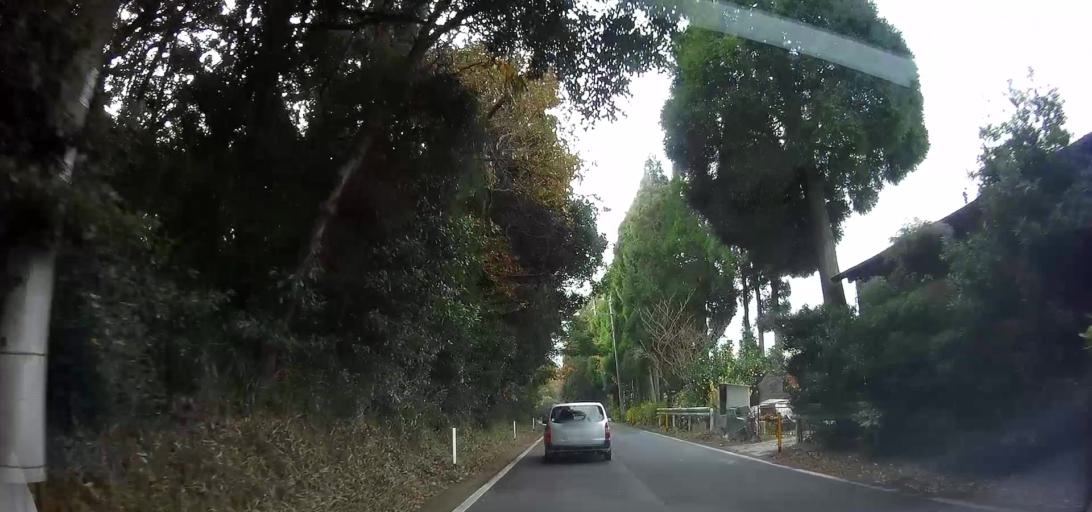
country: JP
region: Nagasaki
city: Shimabara
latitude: 32.7000
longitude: 130.2481
